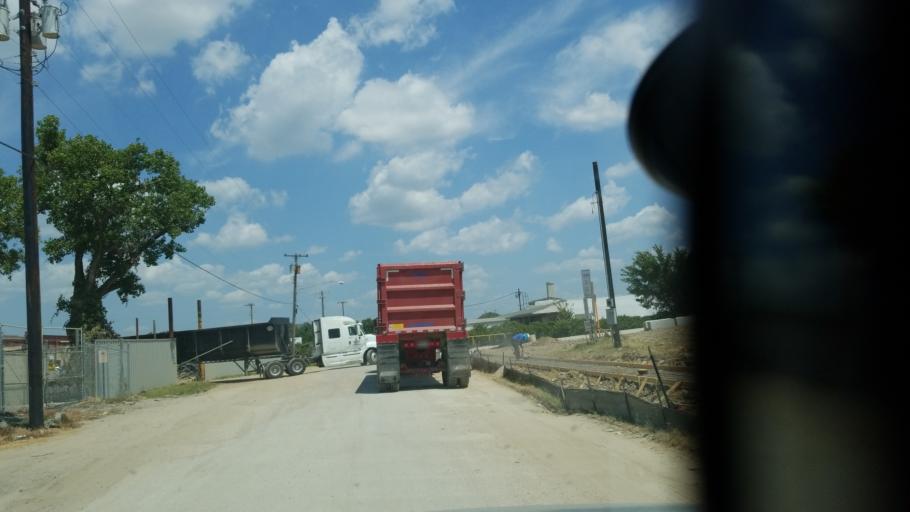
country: US
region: Texas
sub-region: Dallas County
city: Farmers Branch
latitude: 32.8761
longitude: -96.9177
